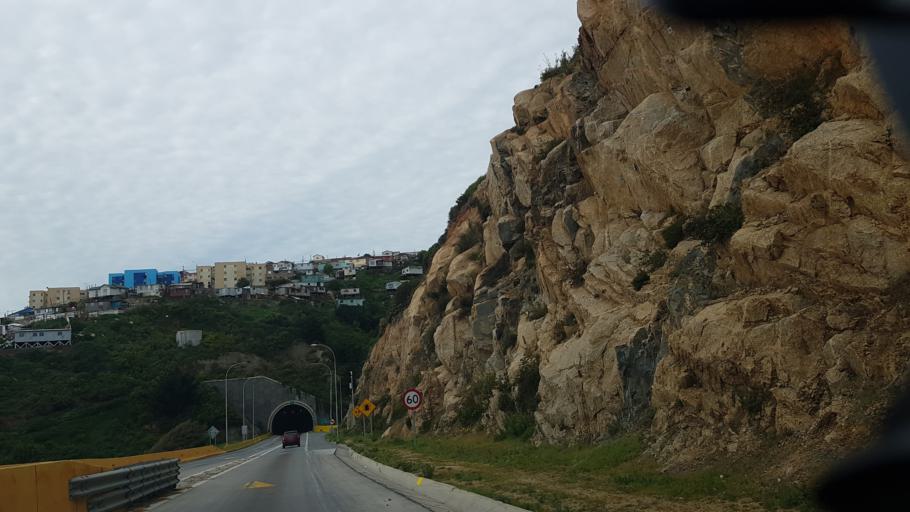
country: CL
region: Valparaiso
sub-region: Provincia de Valparaiso
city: Valparaiso
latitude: -33.0471
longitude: -71.6565
